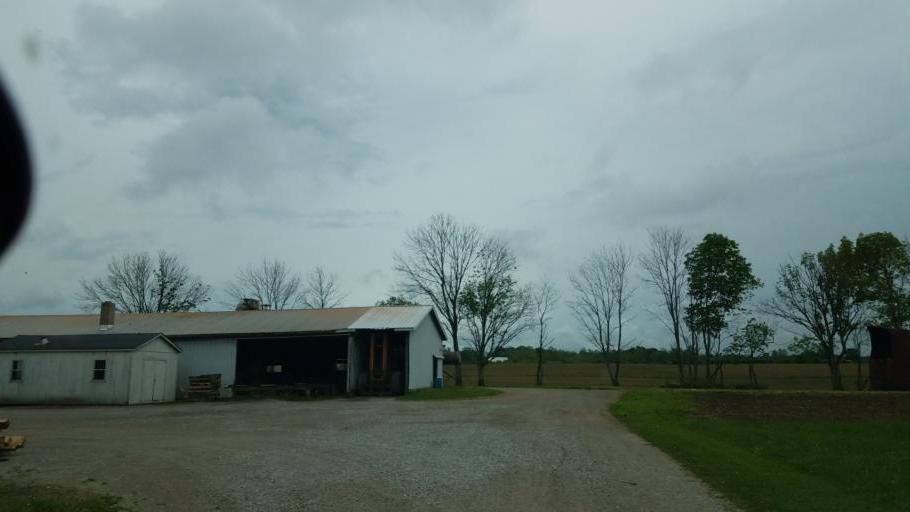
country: US
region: Ohio
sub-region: Richland County
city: Lexington
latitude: 40.6215
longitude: -82.6270
